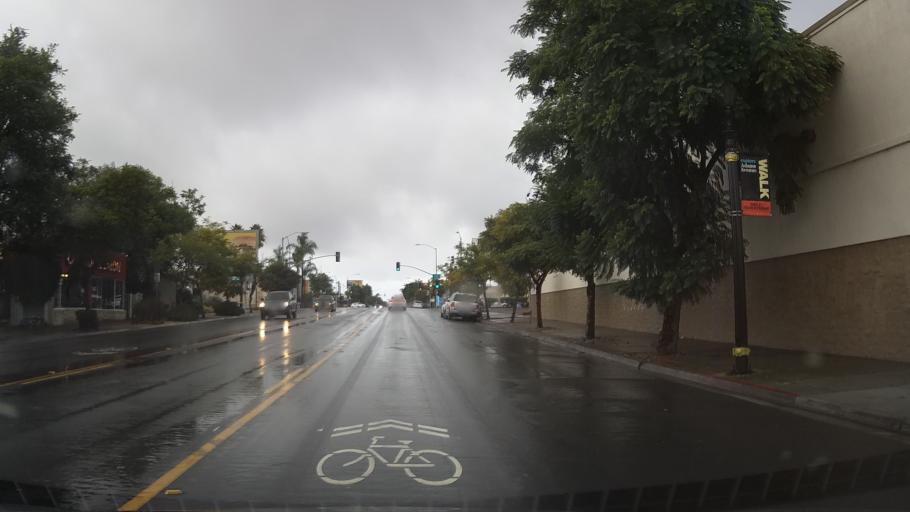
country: US
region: California
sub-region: San Diego County
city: San Diego
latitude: 32.7634
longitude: -117.1129
